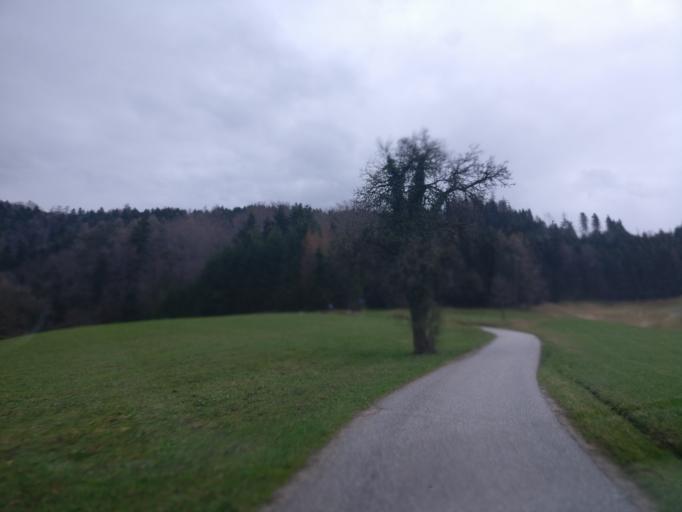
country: AT
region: Salzburg
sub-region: Politischer Bezirk Hallein
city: Golling an der Salzach
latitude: 47.6248
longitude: 13.1765
